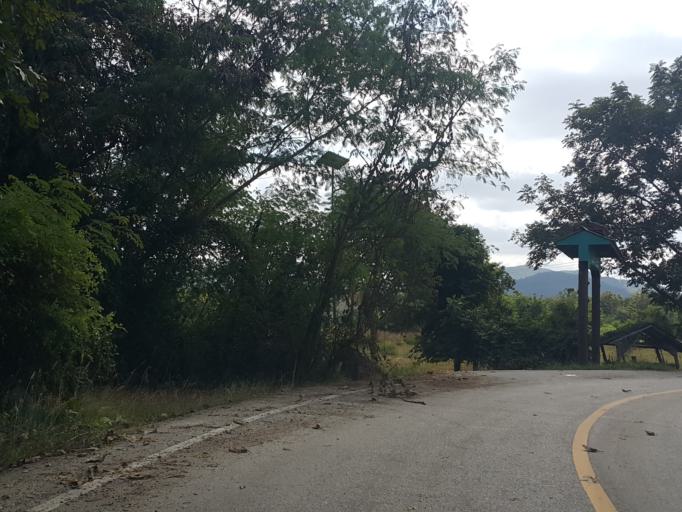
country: TH
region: Lamphun
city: Mae Tha
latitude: 18.5292
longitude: 99.0841
